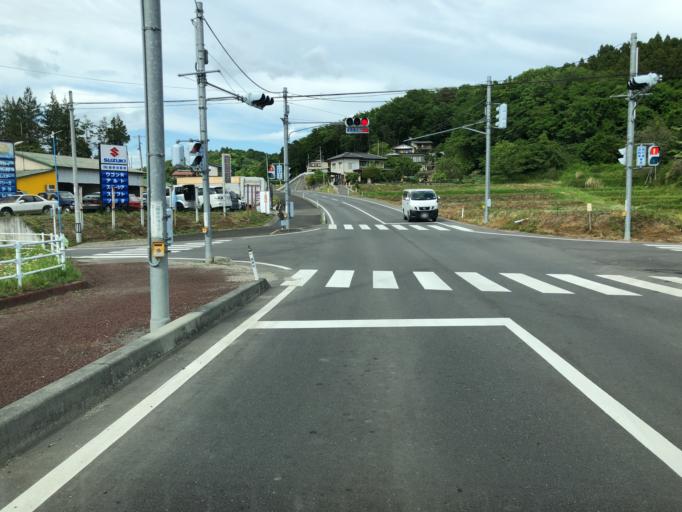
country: JP
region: Fukushima
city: Fukushima-shi
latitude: 37.6522
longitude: 140.5413
